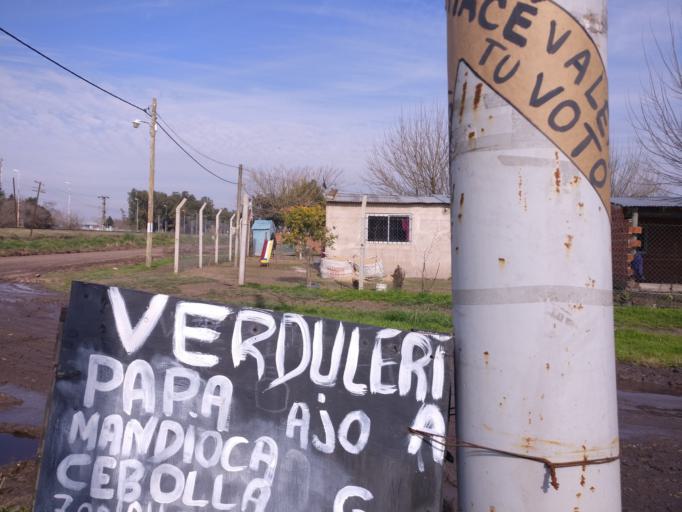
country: AR
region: Buenos Aires
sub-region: Partido de Ezeiza
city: Ezeiza
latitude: -34.9317
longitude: -58.6171
